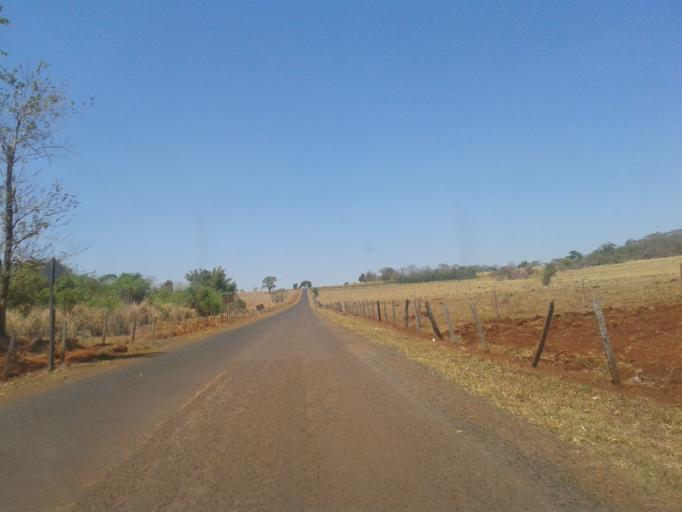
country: BR
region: Minas Gerais
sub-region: Uberlandia
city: Uberlandia
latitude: -18.7730
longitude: -48.2966
